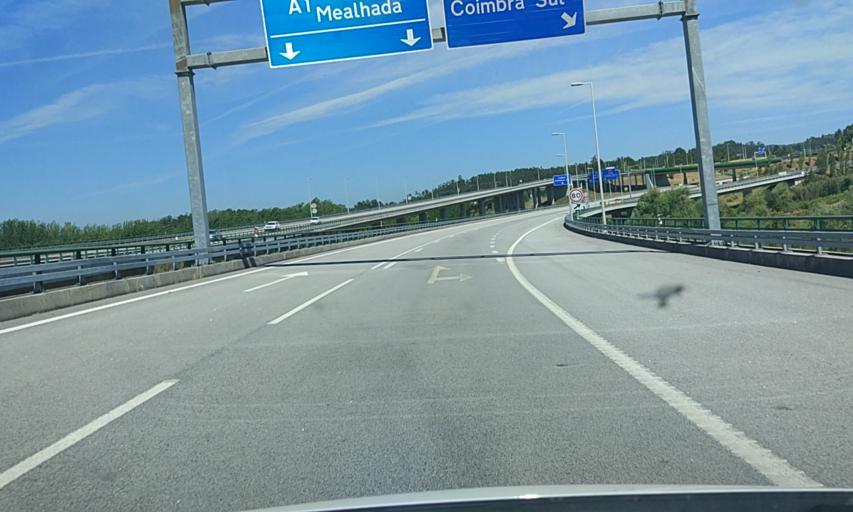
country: PT
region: Aveiro
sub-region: Mealhada
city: Pampilhosa do Botao
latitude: 40.2738
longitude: -8.4887
